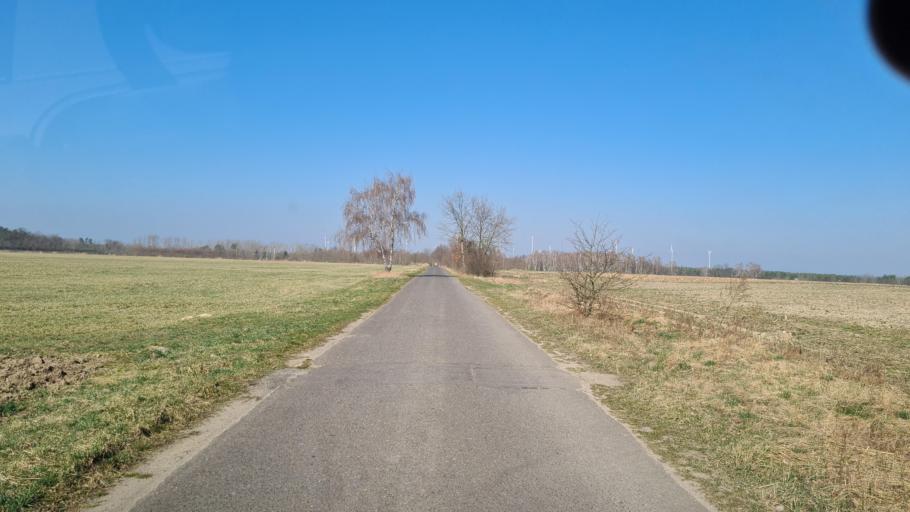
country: DE
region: Brandenburg
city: Calau
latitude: 51.7945
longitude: 13.9871
